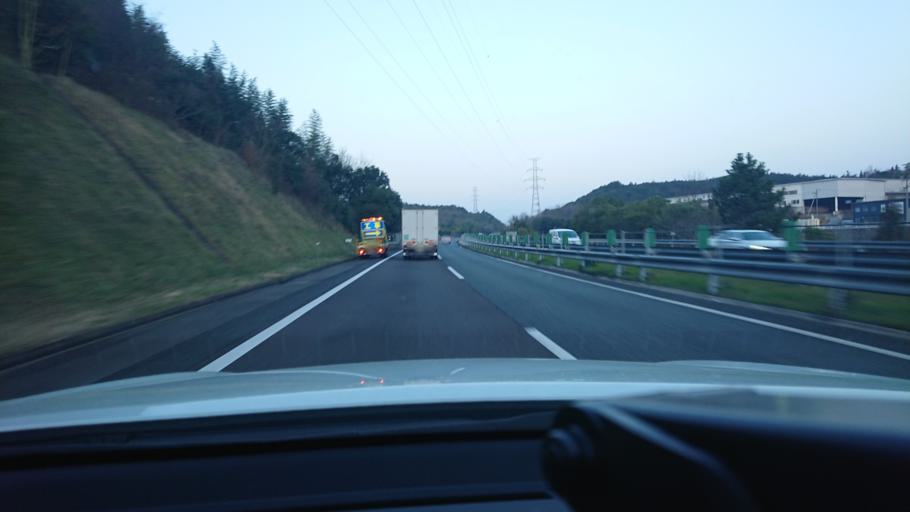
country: JP
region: Kagawa
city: Takamatsu-shi
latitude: 34.2698
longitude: 133.9460
